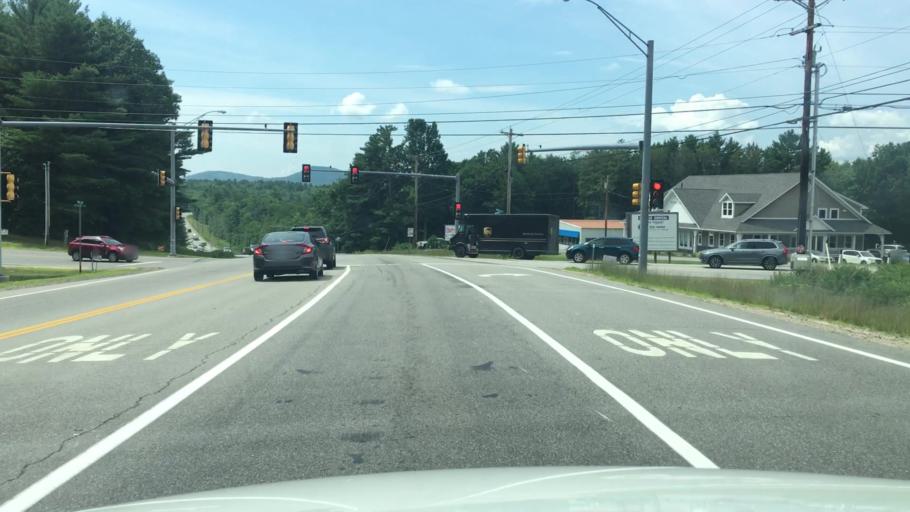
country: US
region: New Hampshire
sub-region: Belknap County
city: Meredith
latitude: 43.6394
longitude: -71.5296
